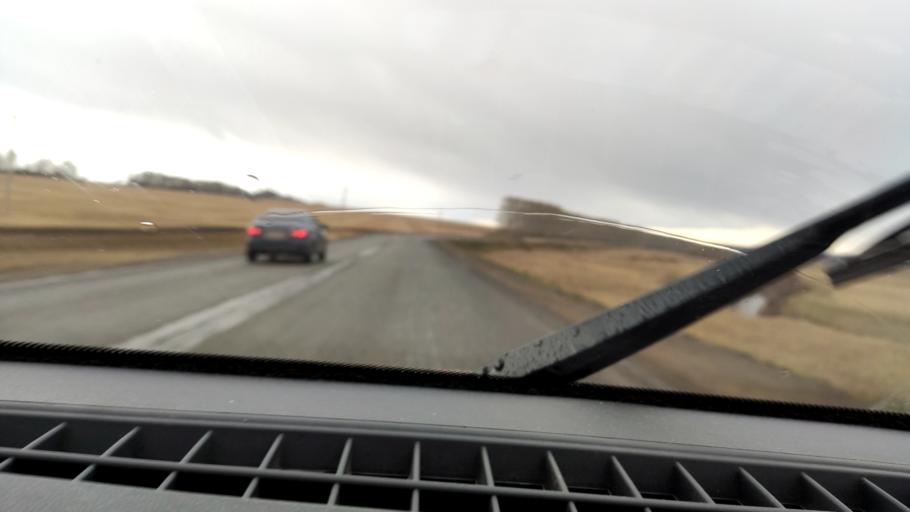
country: RU
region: Bashkortostan
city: Chekmagush
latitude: 55.1179
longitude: 54.7834
